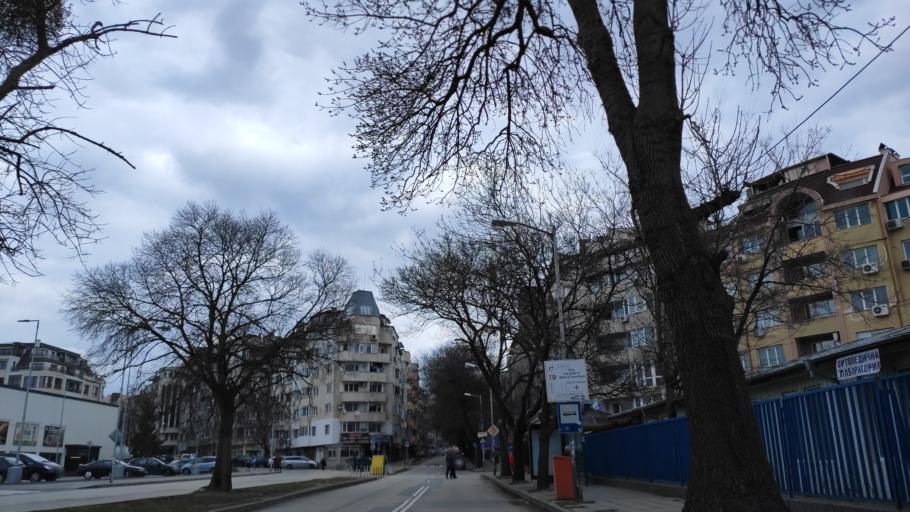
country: BG
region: Varna
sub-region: Obshtina Varna
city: Varna
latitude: 43.2145
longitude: 27.9155
